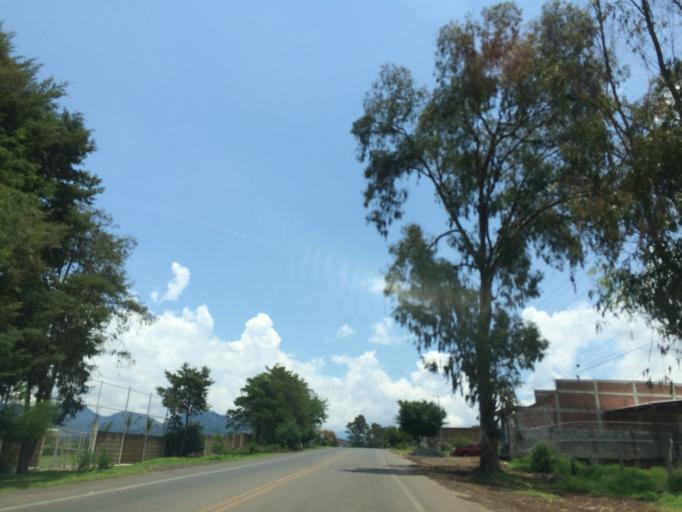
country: MX
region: Michoacan
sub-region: Periban
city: San Francisco Periban
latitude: 19.5494
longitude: -102.4042
